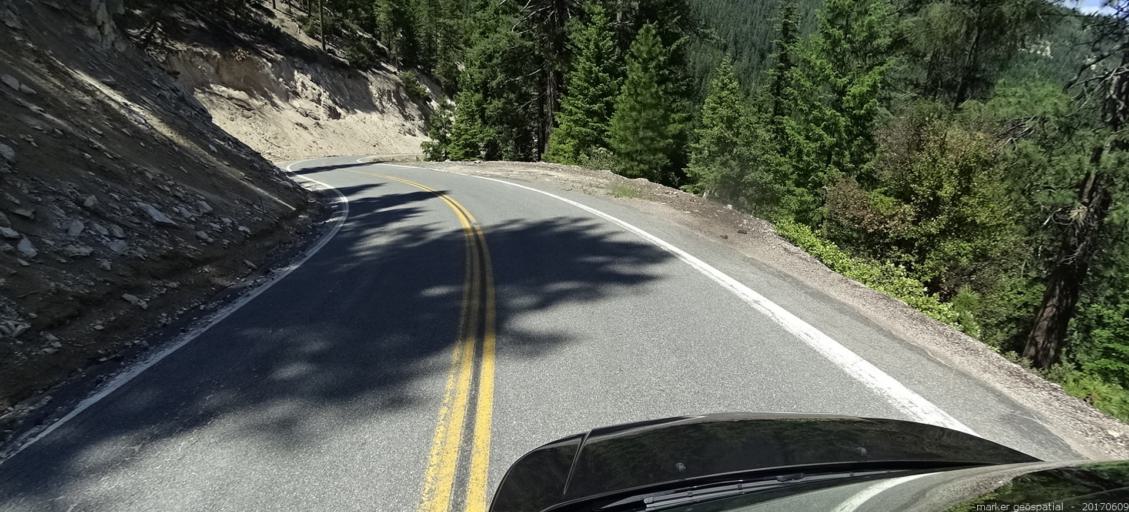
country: US
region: California
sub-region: Siskiyou County
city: Yreka
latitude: 41.4243
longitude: -122.9615
